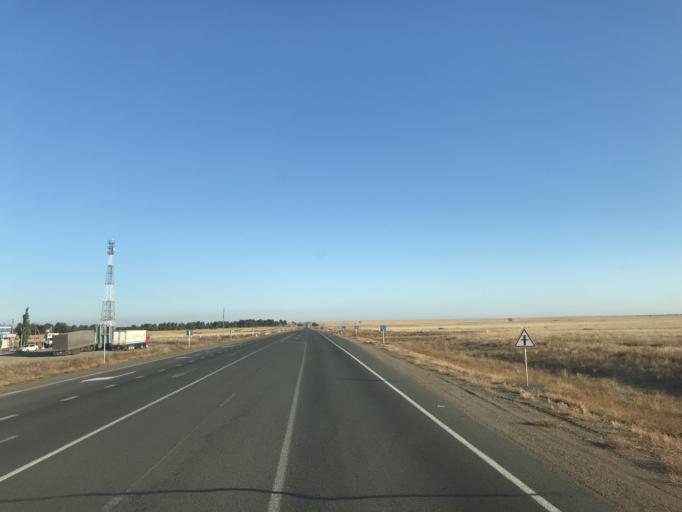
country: KZ
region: Pavlodar
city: Kurchatov
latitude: 51.1881
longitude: 78.6972
